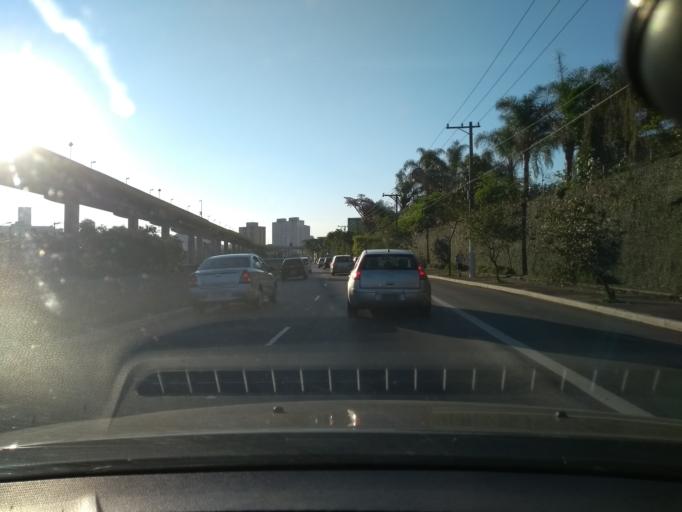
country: BR
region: Sao Paulo
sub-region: Sao Paulo
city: Sao Paulo
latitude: -23.5705
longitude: -46.6046
